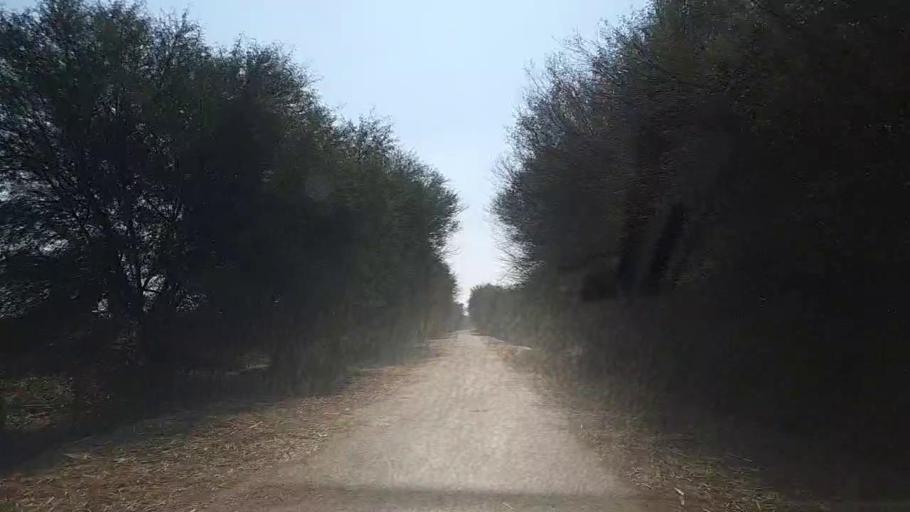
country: PK
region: Sindh
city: Daur
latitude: 26.5075
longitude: 68.3402
